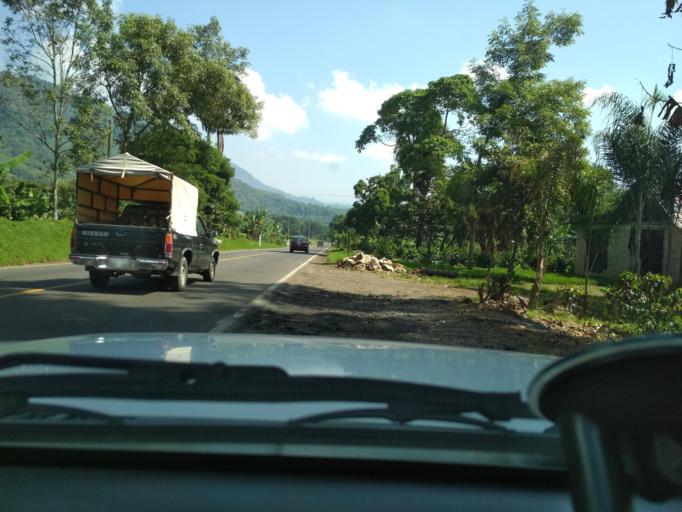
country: MX
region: Veracruz
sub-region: Fortin
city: Santa Lucia Potrerillo
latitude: 18.9780
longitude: -97.0167
